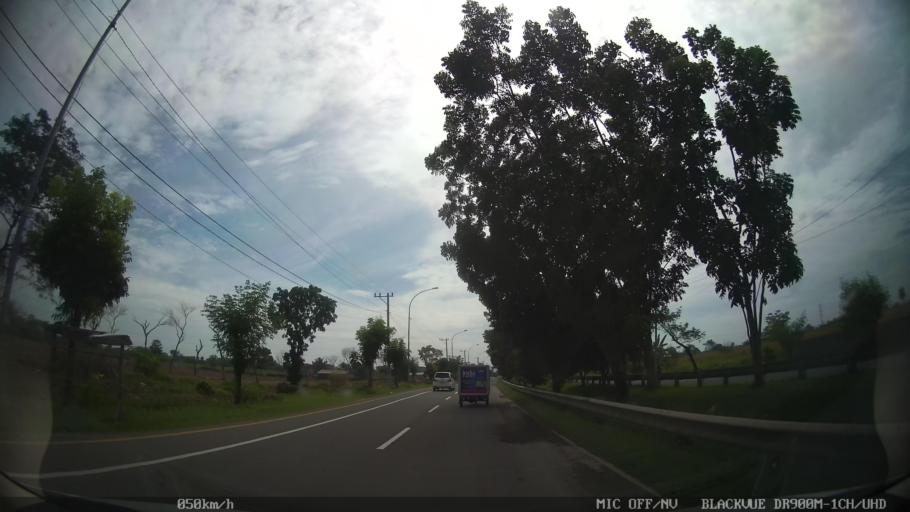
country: ID
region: North Sumatra
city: Percut
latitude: 3.5982
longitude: 98.8115
